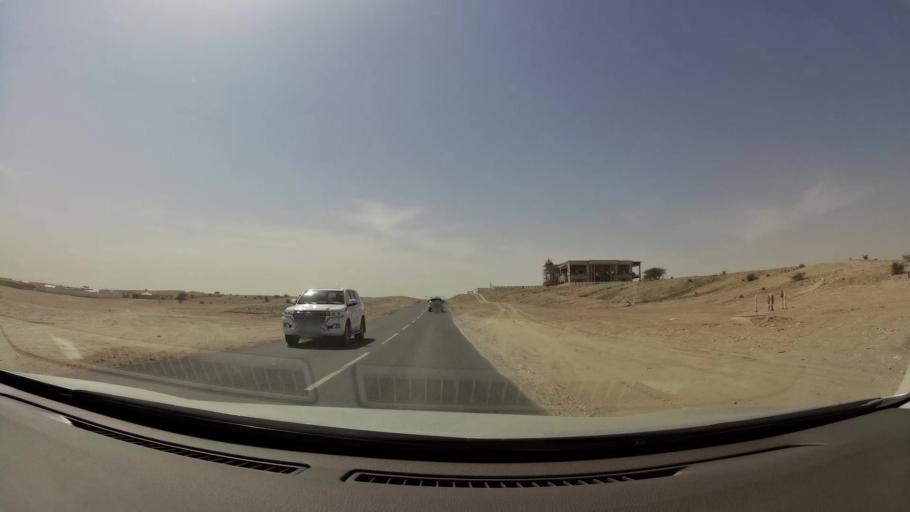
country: QA
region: Baladiyat ar Rayyan
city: Ar Rayyan
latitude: 25.2642
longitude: 51.3958
